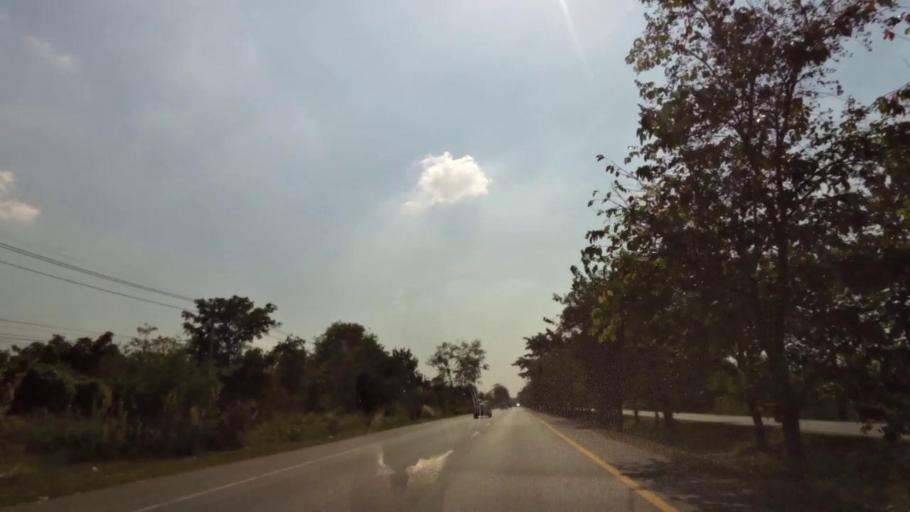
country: TH
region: Phichit
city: Bueng Na Rang
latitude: 16.1678
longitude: 100.1268
